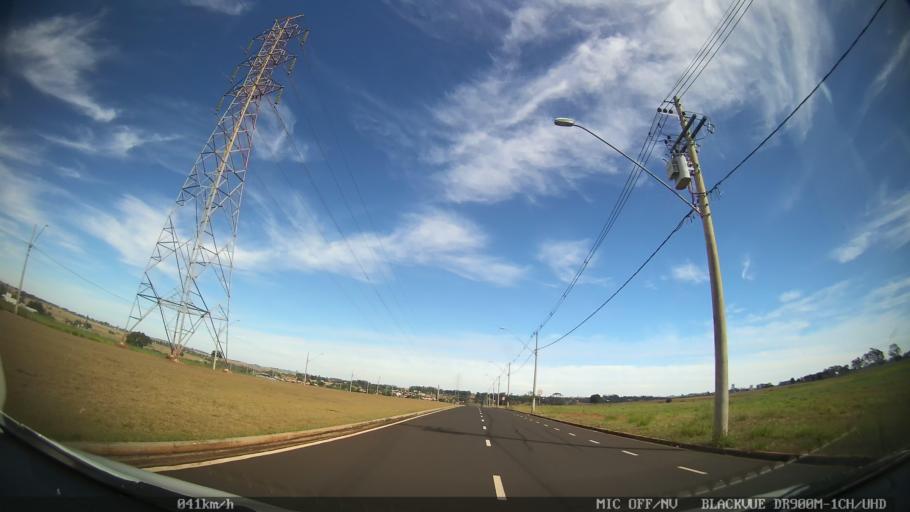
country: BR
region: Sao Paulo
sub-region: Sao Jose Do Rio Preto
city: Sao Jose do Rio Preto
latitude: -20.8523
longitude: -49.3764
